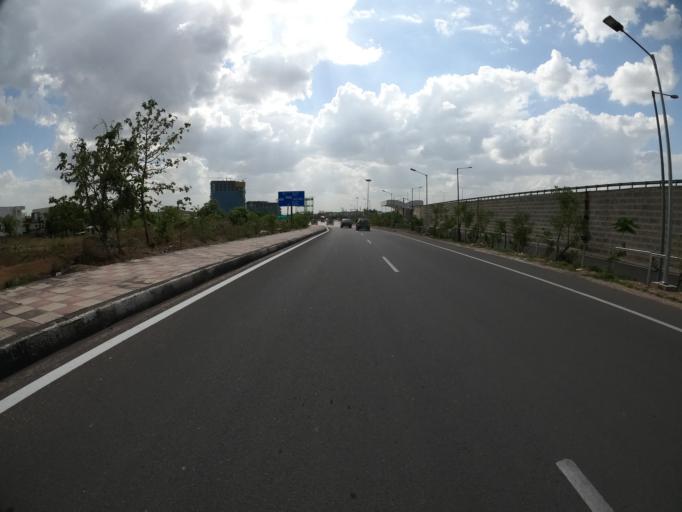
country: IN
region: Telangana
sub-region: Medak
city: Serilingampalle
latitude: 17.4059
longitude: 78.3317
